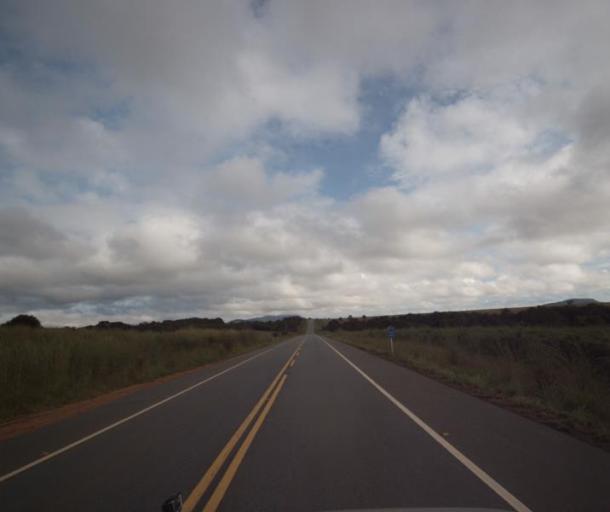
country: BR
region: Goias
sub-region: Padre Bernardo
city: Padre Bernardo
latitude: -15.3038
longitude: -48.6691
